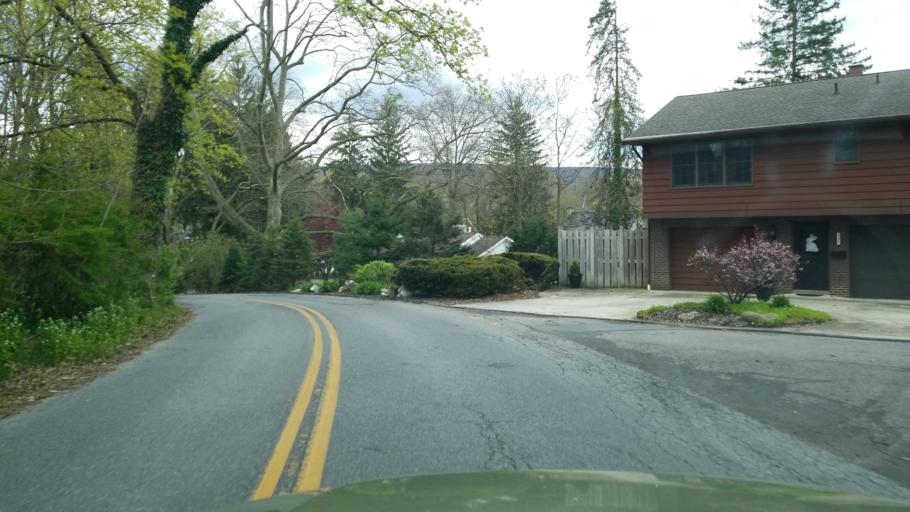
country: US
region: Pennsylvania
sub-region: Blair County
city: Lakemont
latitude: 40.4915
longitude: -78.4078
